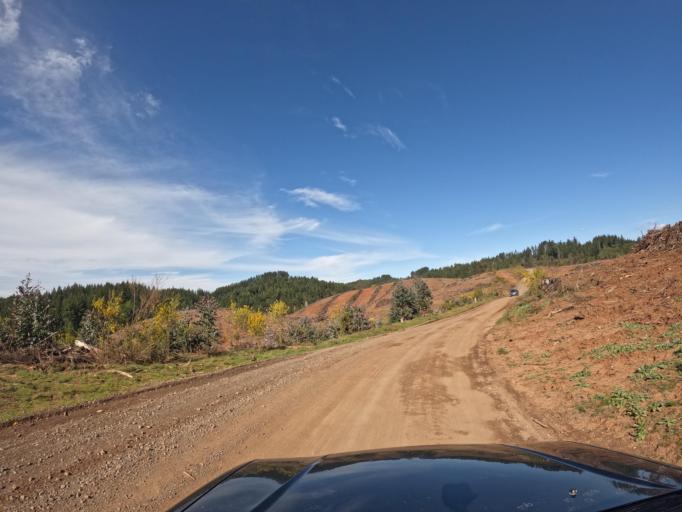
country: CL
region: Biobio
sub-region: Provincia de Biobio
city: La Laja
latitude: -37.0858
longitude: -72.8319
